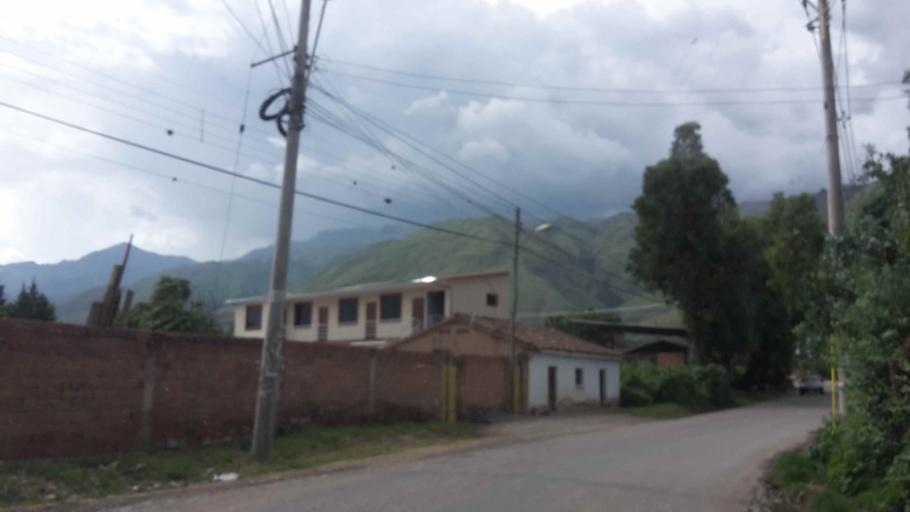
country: BO
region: Cochabamba
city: Cochabamba
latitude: -17.3314
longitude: -66.2405
